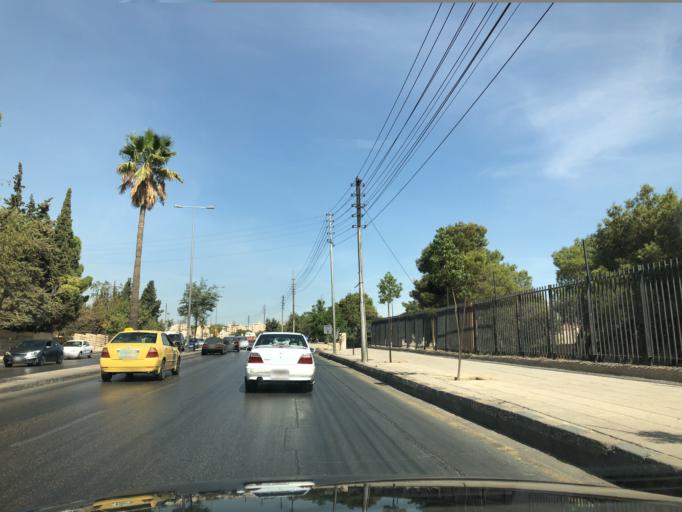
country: JO
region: Amman
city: Amman
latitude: 31.9806
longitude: 35.9023
